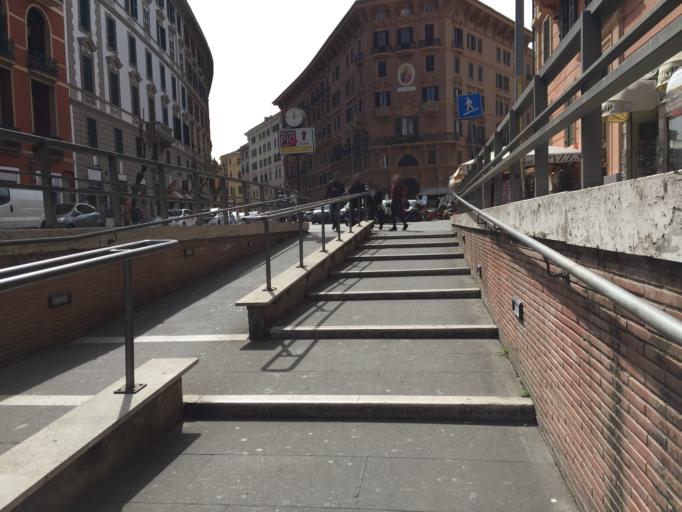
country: VA
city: Vatican City
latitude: 41.8999
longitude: 12.4564
